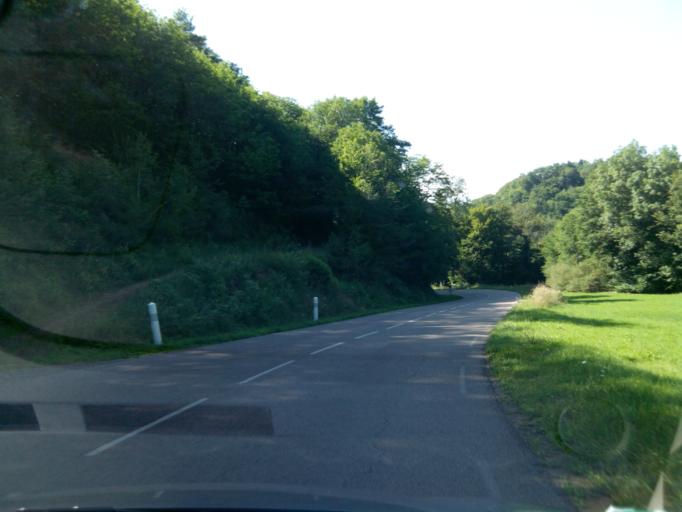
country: FR
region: Limousin
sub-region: Departement de la Correze
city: Beynat
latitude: 45.1185
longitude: 1.7077
